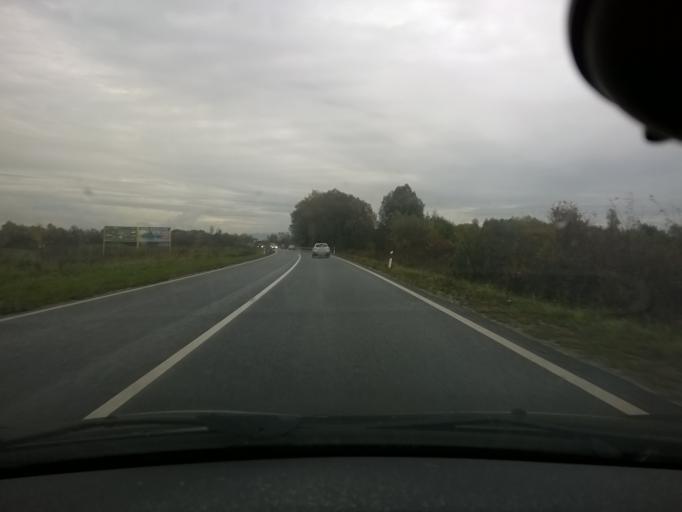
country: HR
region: Zagrebacka
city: Jakovlje
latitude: 45.9637
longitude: 15.8431
